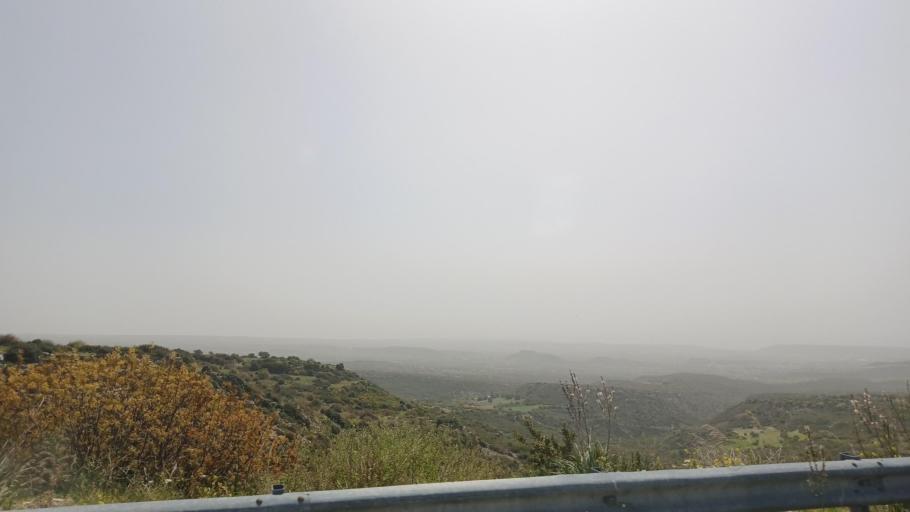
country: CY
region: Limassol
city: Pissouri
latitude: 34.7238
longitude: 32.7288
